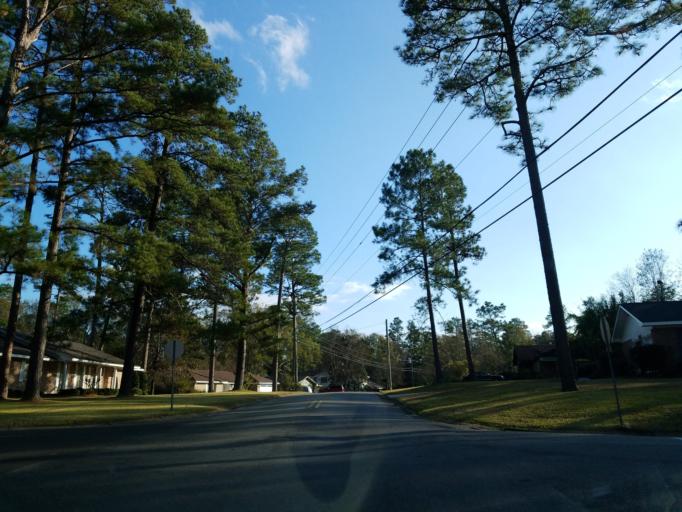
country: US
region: Mississippi
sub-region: Lamar County
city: West Hattiesburg
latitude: 31.3167
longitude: -89.3400
